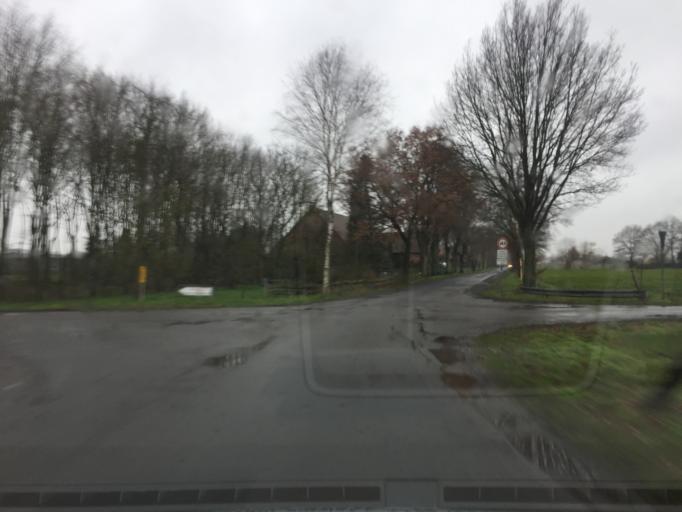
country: DE
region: Lower Saxony
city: Borstel
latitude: 52.6033
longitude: 8.9503
